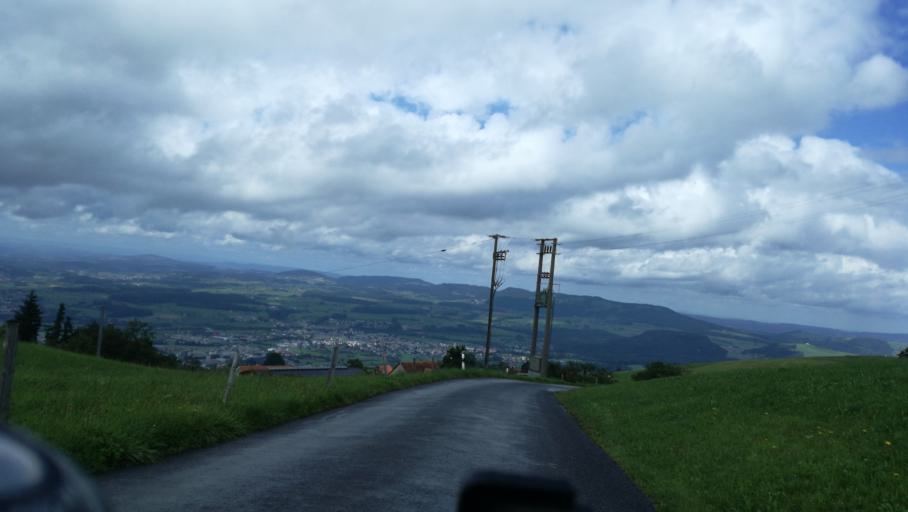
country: CH
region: Zug
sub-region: Zug
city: Zug
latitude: 47.1510
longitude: 8.5375
